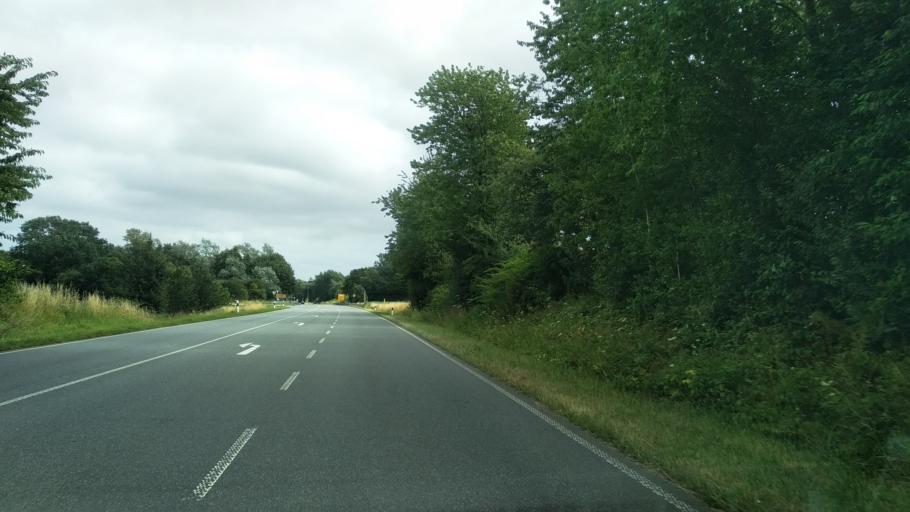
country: DE
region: Schleswig-Holstein
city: Schleswig
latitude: 54.5375
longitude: 9.5546
